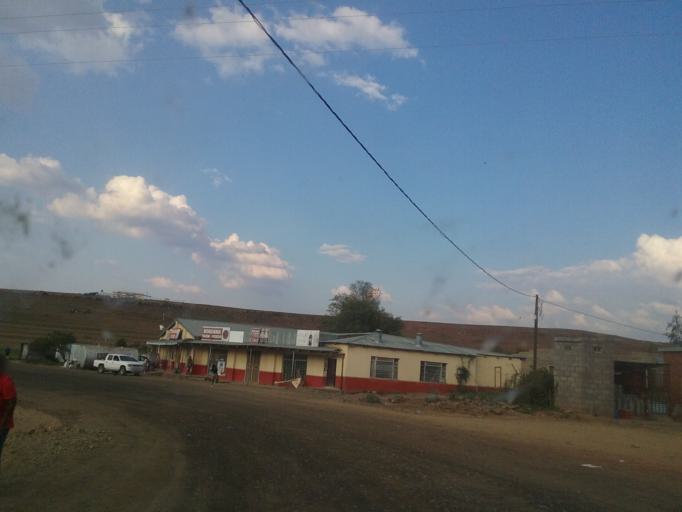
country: LS
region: Quthing
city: Quthing
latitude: -30.3952
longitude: 27.6257
